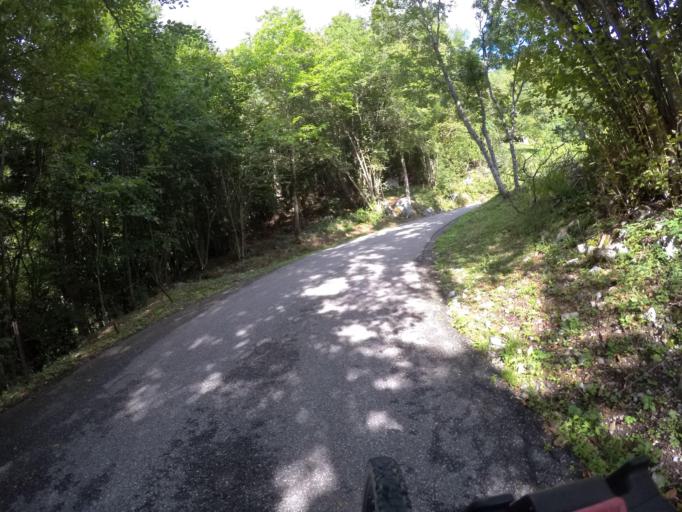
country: IT
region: Friuli Venezia Giulia
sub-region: Provincia di Udine
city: Moggio Udinese
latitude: 46.4847
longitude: 13.1885
